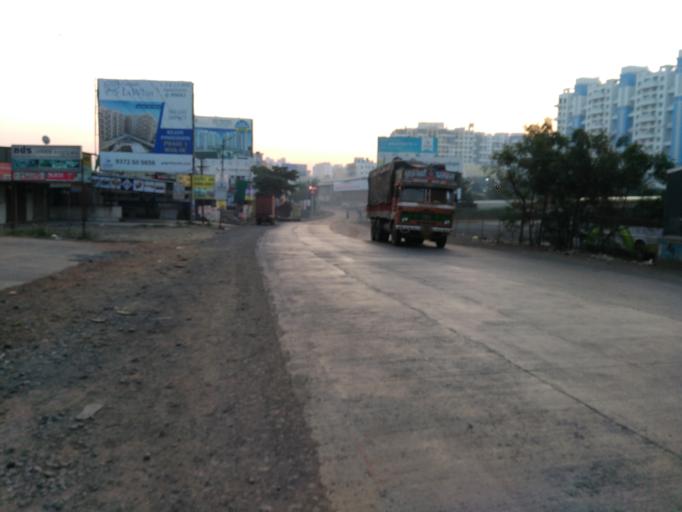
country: IN
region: Maharashtra
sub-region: Pune Division
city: Pune
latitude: 18.4495
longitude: 73.9031
